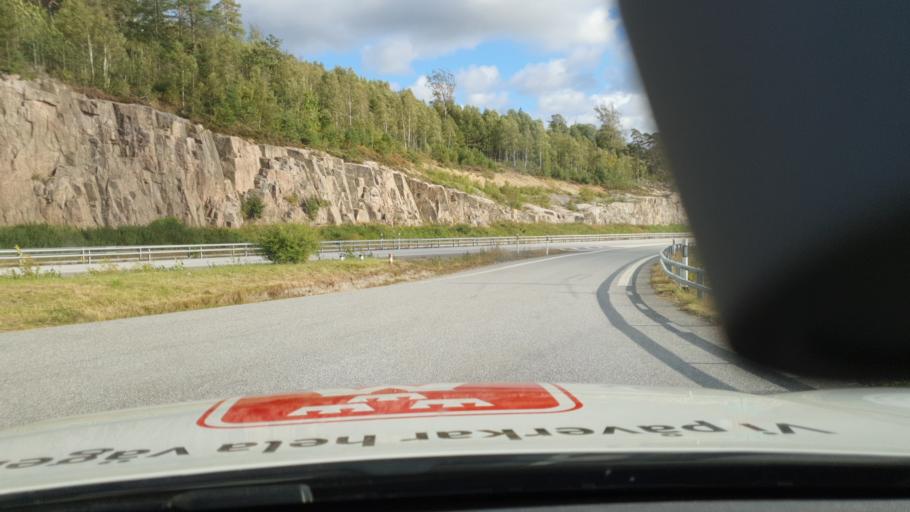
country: SE
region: Vaestra Goetaland
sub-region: Stromstads Kommun
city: Stroemstad
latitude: 59.0020
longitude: 11.2313
